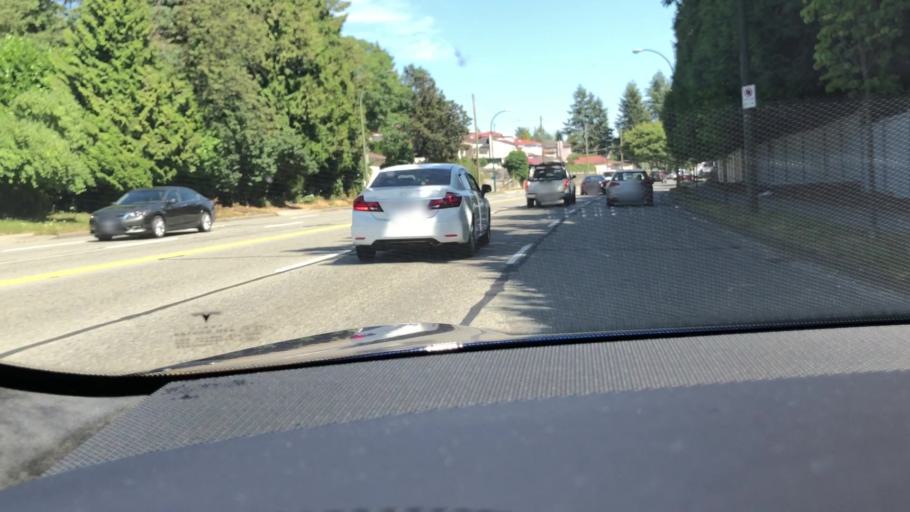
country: CA
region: British Columbia
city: Vancouver
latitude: 49.2111
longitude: -123.0700
